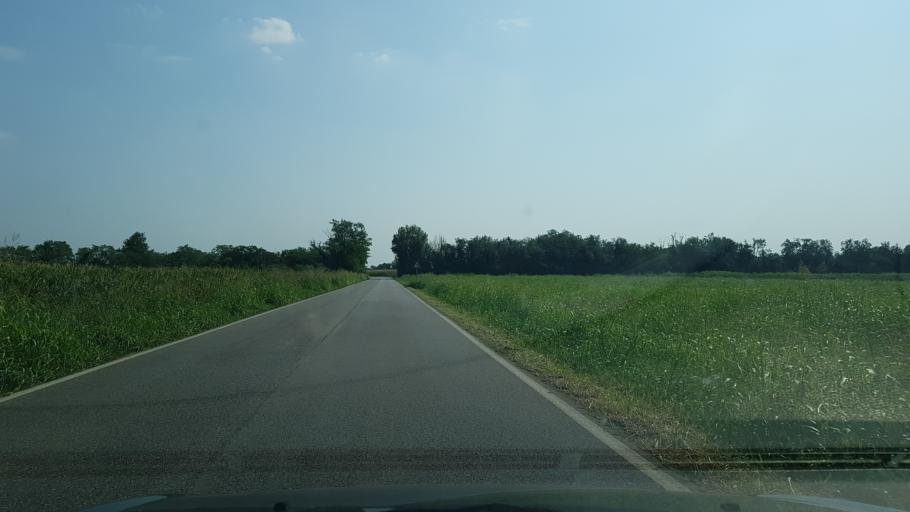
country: IT
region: Friuli Venezia Giulia
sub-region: Provincia di Udine
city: San Vito di Fagagna
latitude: 46.0811
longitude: 13.0755
